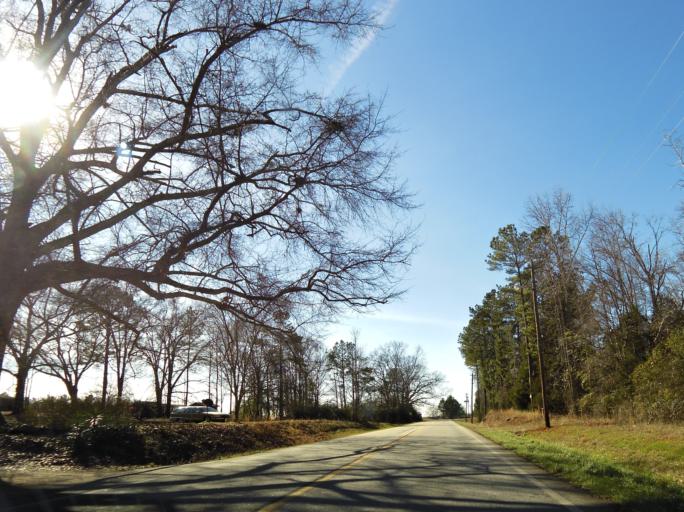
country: US
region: Georgia
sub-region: Lamar County
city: Barnesville
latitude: 32.9125
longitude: -84.1496
